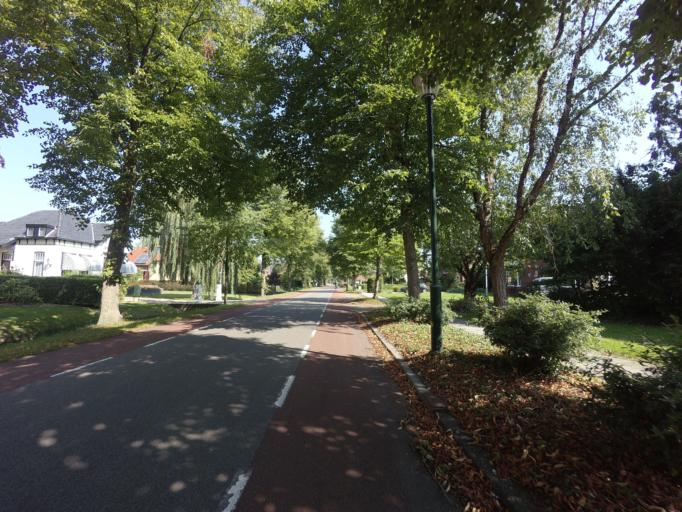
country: NL
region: Groningen
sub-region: Gemeente Zuidhorn
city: Grijpskerk
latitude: 53.2637
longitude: 6.3145
